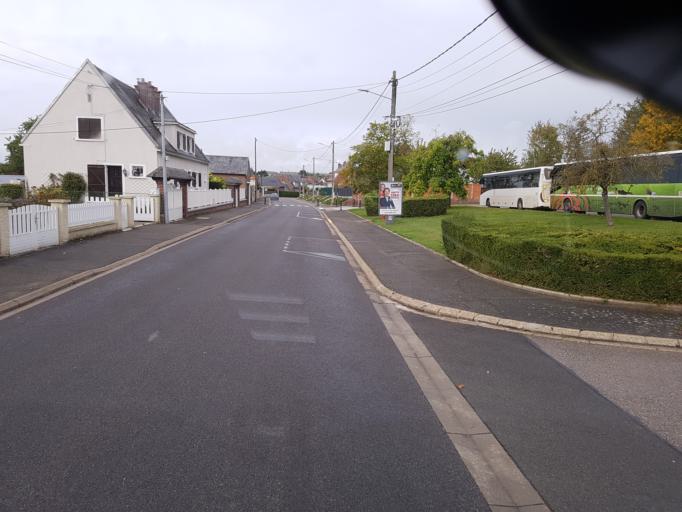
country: FR
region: Picardie
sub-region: Departement de l'Oise
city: Breteuil
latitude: 49.6349
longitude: 2.2997
